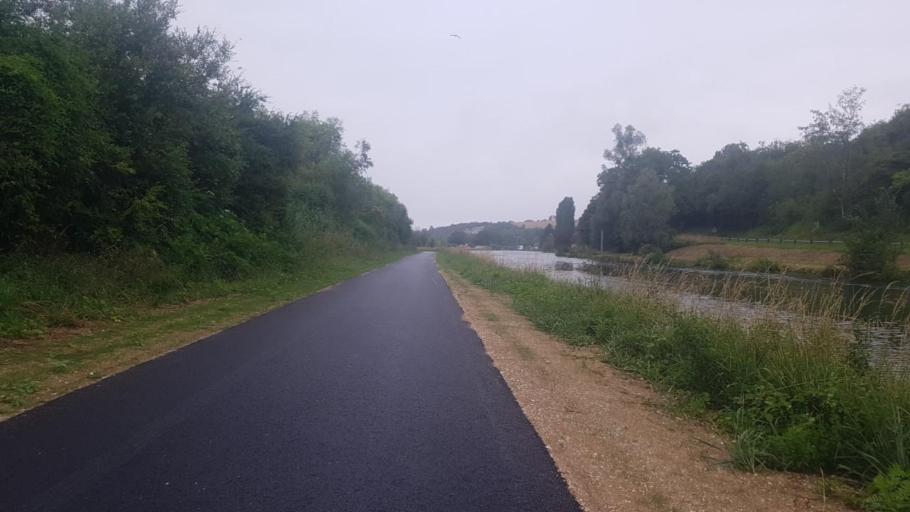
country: FR
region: Champagne-Ardenne
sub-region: Departement de la Marne
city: Vitry-le-Francois
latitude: 48.7861
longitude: 4.5358
